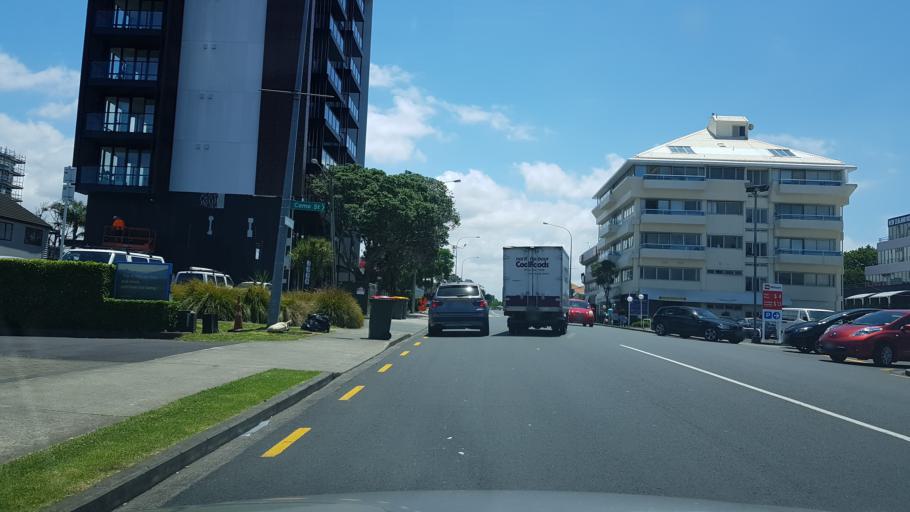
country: NZ
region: Auckland
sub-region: Auckland
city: North Shore
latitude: -36.7892
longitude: 174.7690
